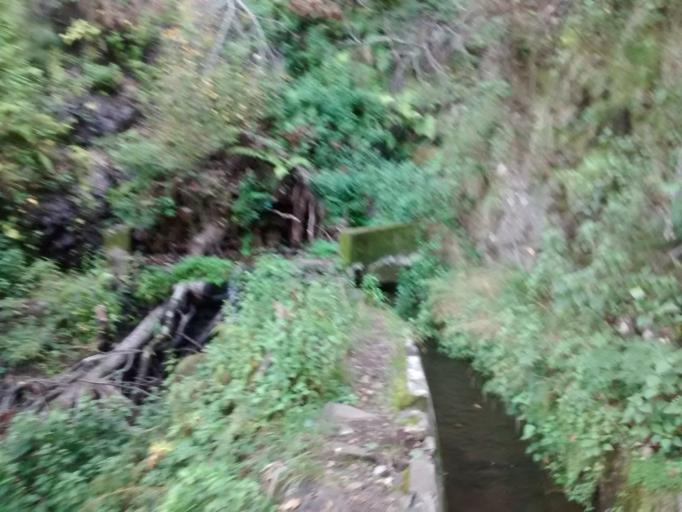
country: PT
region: Madeira
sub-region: Camara de Lobos
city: Curral das Freiras
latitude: 32.7239
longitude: -17.0214
